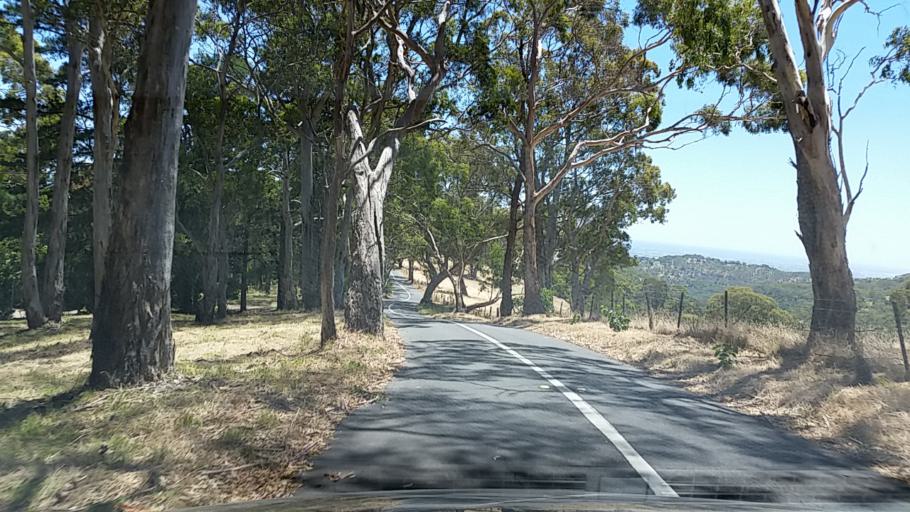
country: AU
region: South Australia
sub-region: Adelaide Hills
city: Upper Sturt
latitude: -34.9993
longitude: 138.6747
